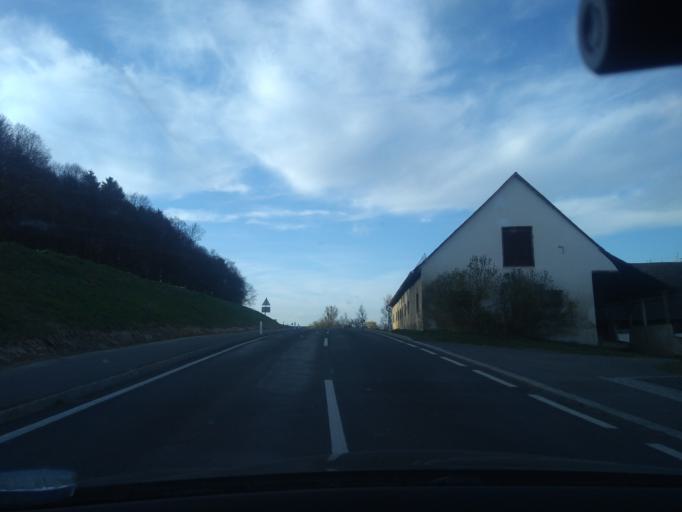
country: AT
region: Styria
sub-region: Politischer Bezirk Suedoststeiermark
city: Sankt Stefan im Rosental
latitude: 46.8921
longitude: 15.7178
